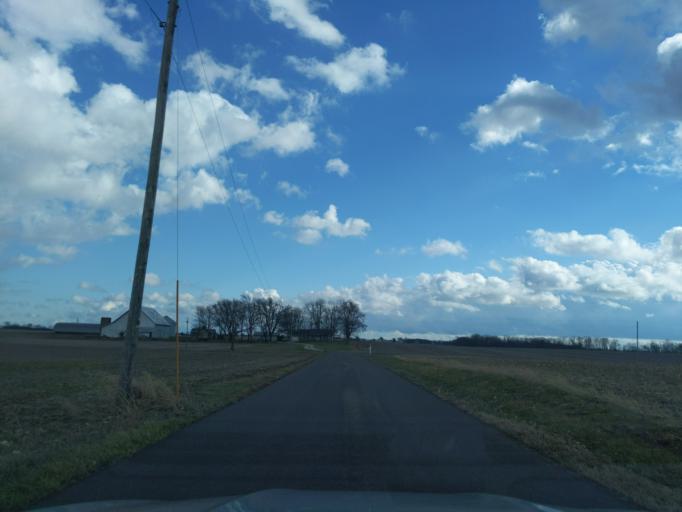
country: US
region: Indiana
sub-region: Decatur County
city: Greensburg
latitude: 39.3804
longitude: -85.5047
